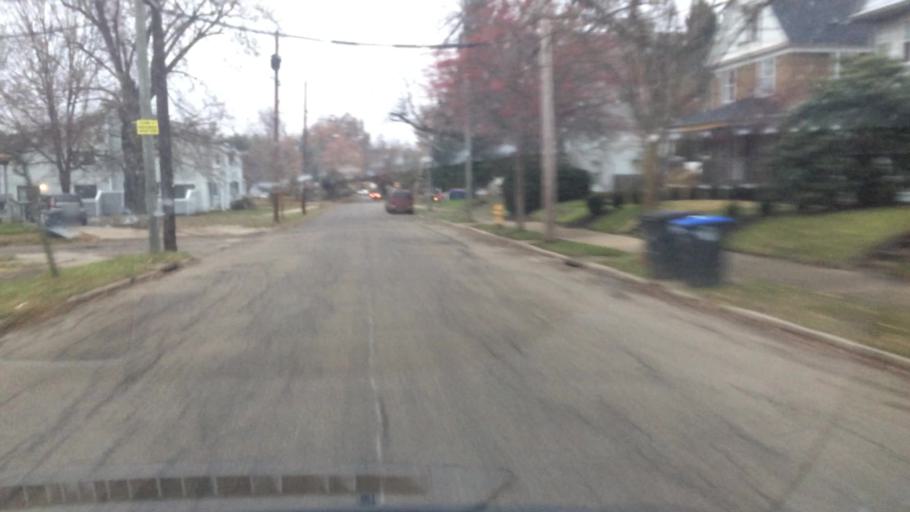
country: US
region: Ohio
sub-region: Summit County
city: Akron
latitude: 41.0647
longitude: -81.5343
